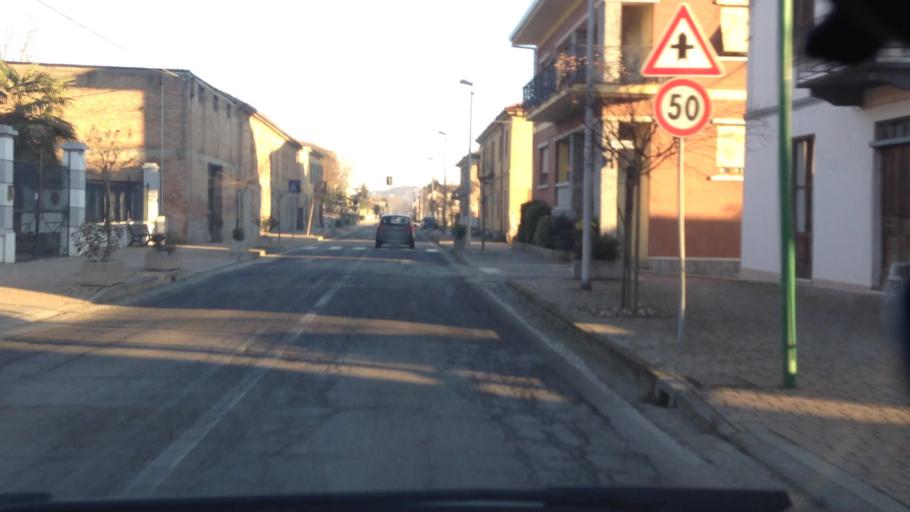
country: IT
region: Piedmont
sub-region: Provincia di Asti
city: Montegrosso
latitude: 44.8184
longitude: 8.2426
